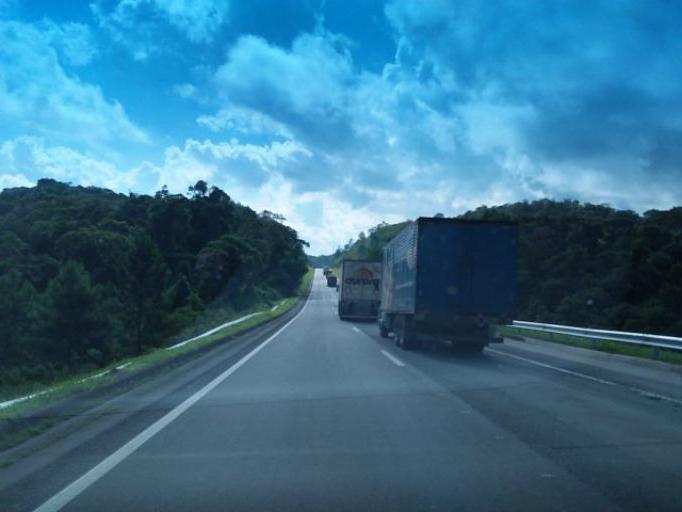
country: BR
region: Parana
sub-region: Antonina
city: Antonina
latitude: -25.1076
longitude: -48.7783
